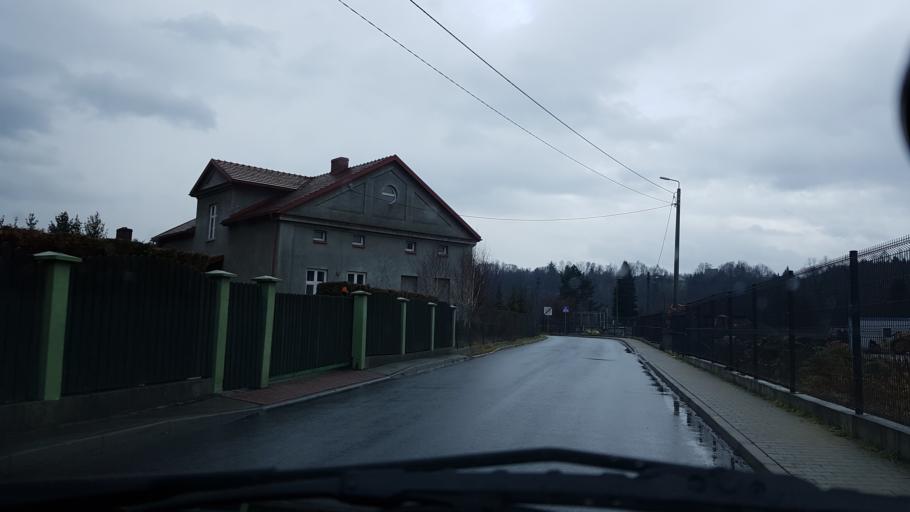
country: PL
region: Lesser Poland Voivodeship
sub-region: Powiat suski
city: Makow Podhalanski
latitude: 49.7282
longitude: 19.6746
